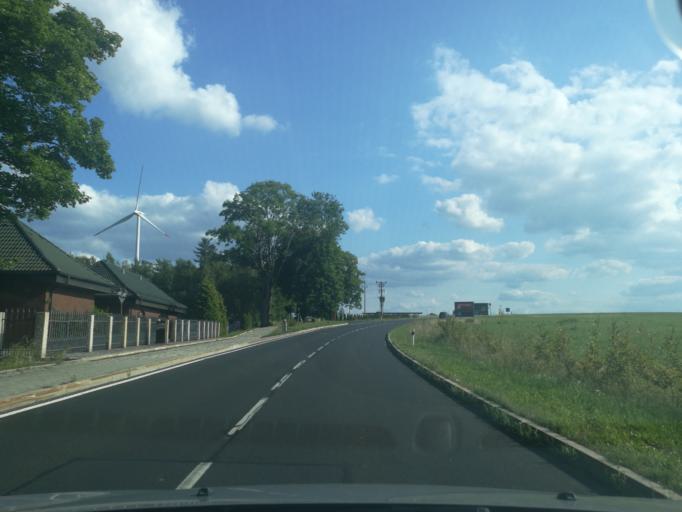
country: CZ
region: Karlovarsky
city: Hranice
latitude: 50.3213
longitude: 12.1660
